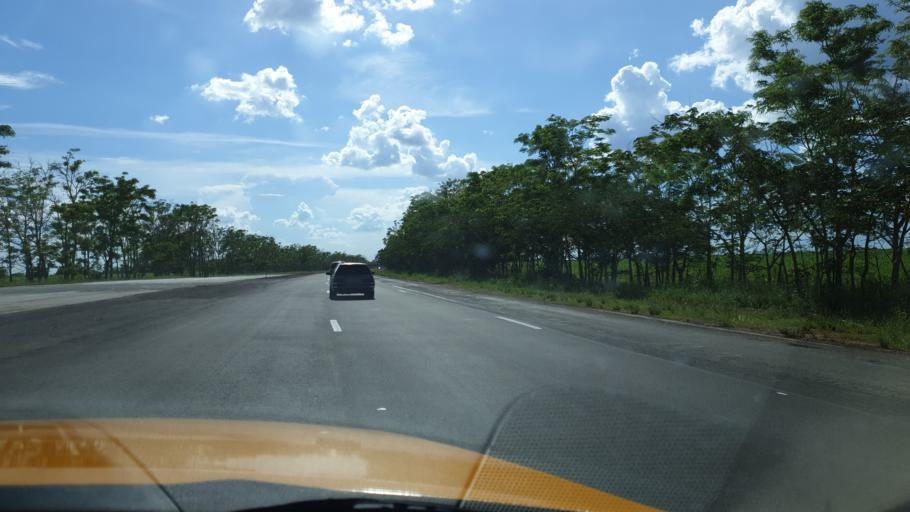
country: CU
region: Cienfuegos
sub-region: Municipio de Aguada de Pasajeros
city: Aguada de Pasajeros
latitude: 22.4021
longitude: -80.8541
